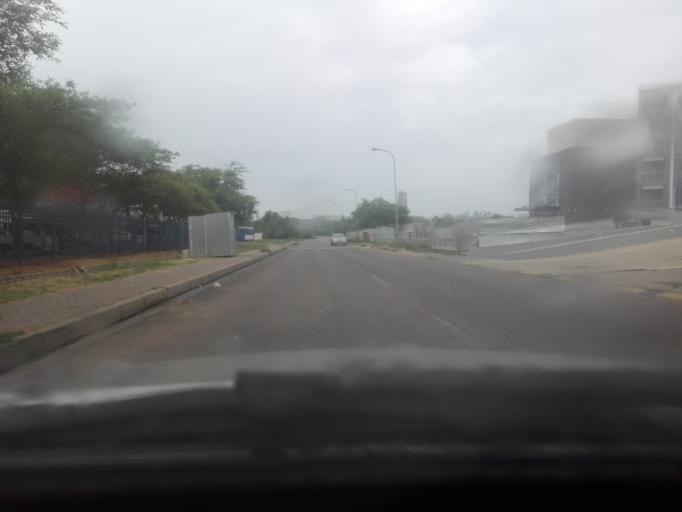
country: BW
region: South East
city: Gaborone
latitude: -24.6368
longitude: 25.8945
